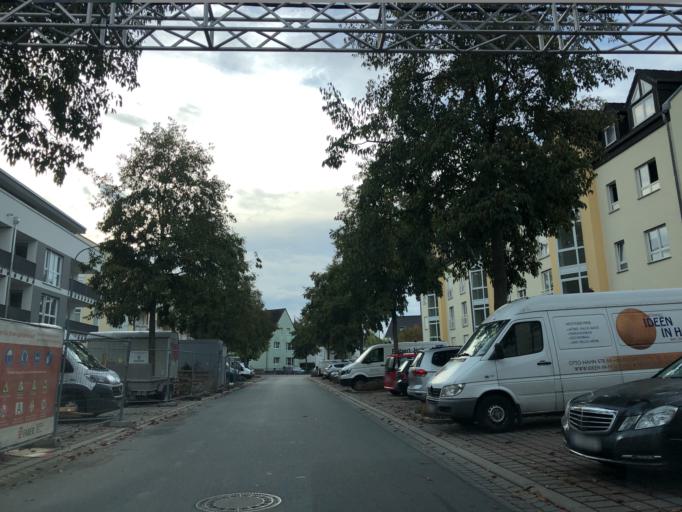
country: DE
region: Hesse
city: Langen
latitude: 49.9939
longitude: 8.6761
